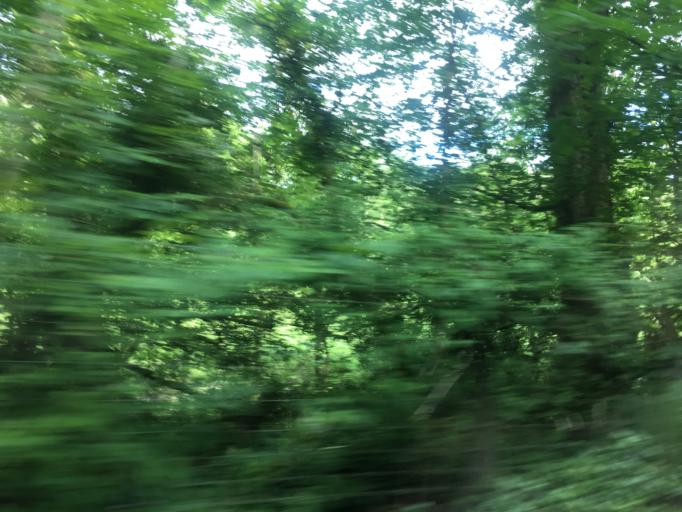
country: GB
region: Wales
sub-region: Carmarthenshire
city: Llansadwrn
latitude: 51.9824
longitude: -3.8880
